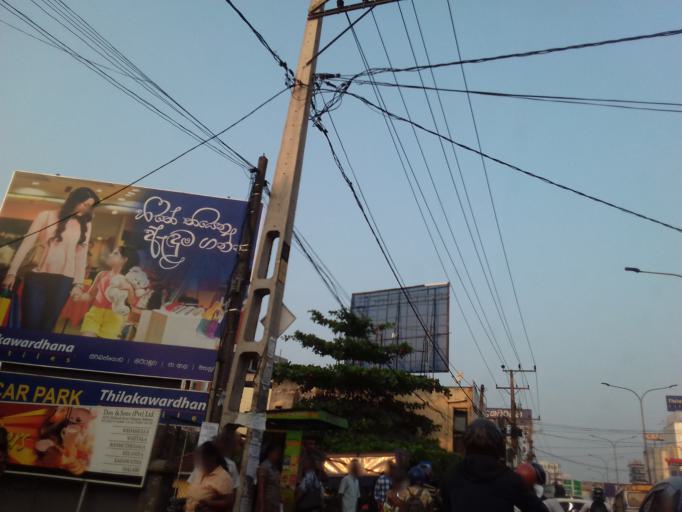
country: LK
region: Western
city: Kelaniya
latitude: 6.9763
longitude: 79.9253
